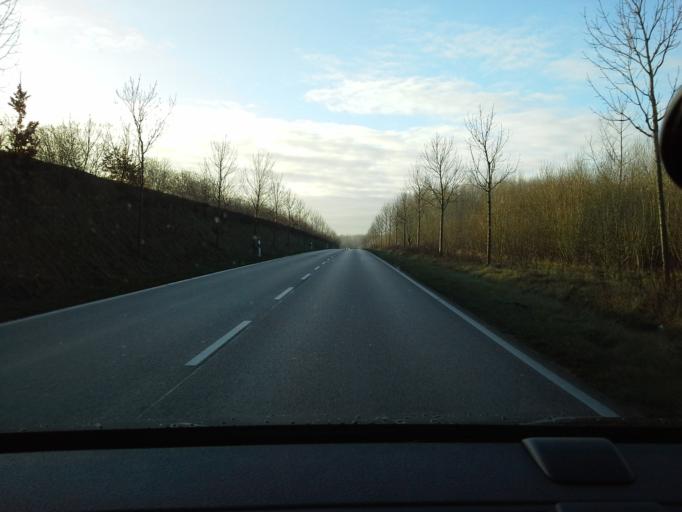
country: DE
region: Schleswig-Holstein
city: Pinneberg
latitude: 53.6554
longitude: 9.7723
